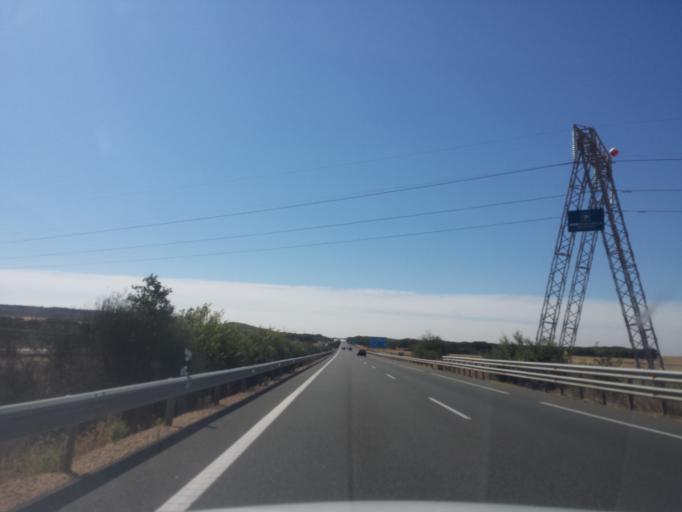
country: ES
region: Castille and Leon
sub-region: Provincia de Valladolid
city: Bercero
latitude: 41.5538
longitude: -5.0788
